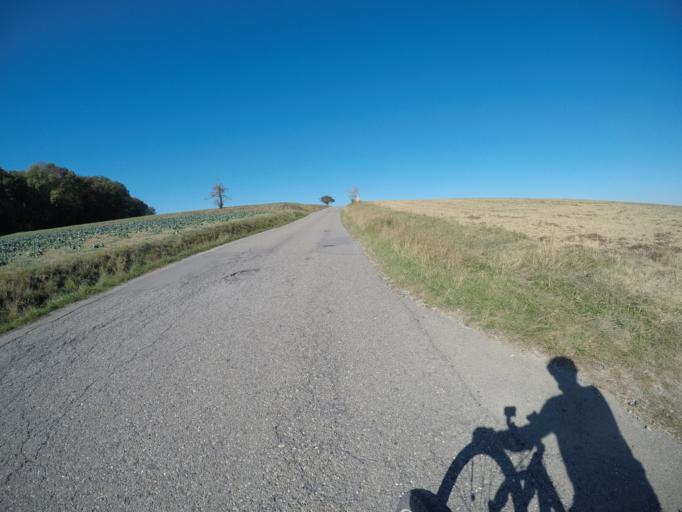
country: DE
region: Baden-Wuerttemberg
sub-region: Regierungsbezirk Stuttgart
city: Herrenberg
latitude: 48.5748
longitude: 8.8413
